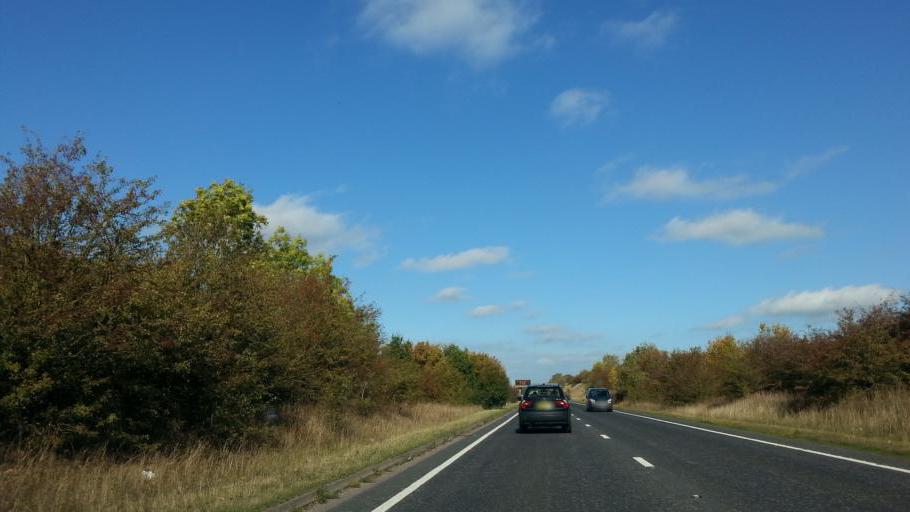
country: GB
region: England
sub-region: Northamptonshire
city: Thrapston
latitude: 52.3767
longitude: -0.5251
